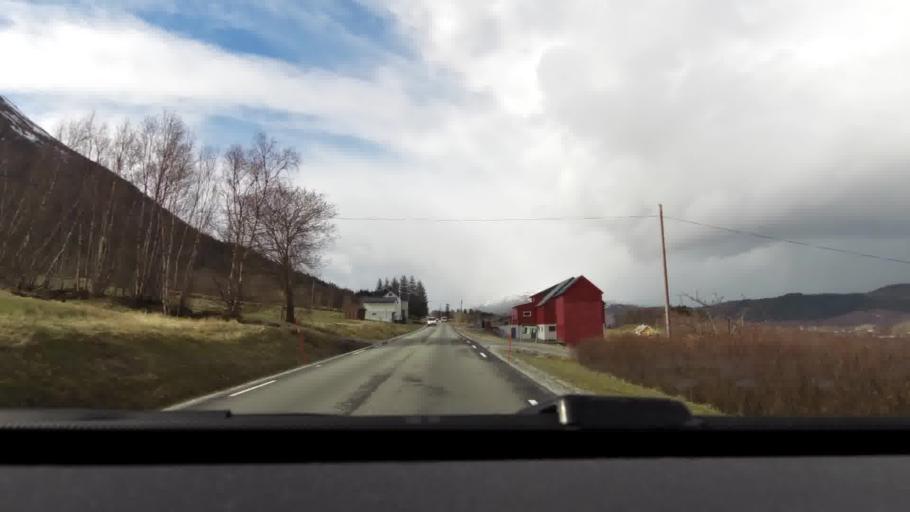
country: NO
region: More og Romsdal
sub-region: Averoy
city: Bruhagen
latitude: 63.1088
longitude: 7.6331
